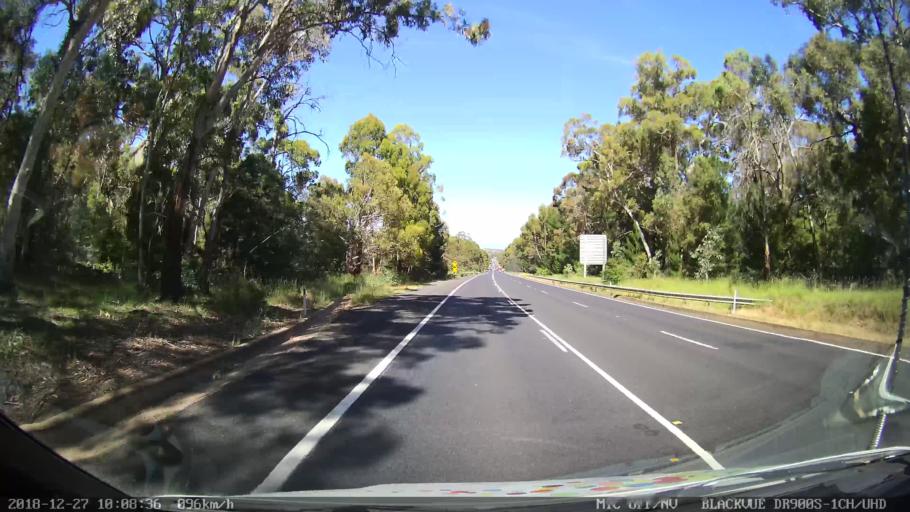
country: AU
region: New South Wales
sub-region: Lithgow
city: Portland
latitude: -33.4485
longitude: 149.8231
